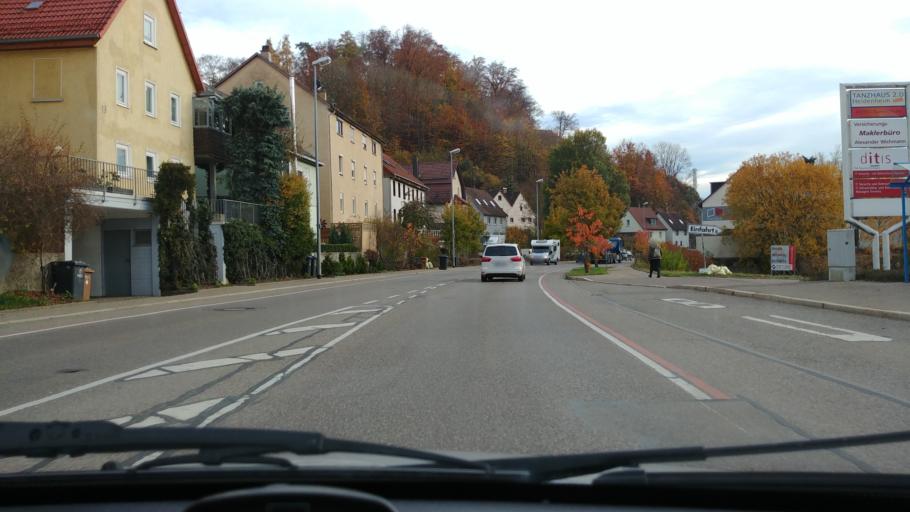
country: DE
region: Baden-Wuerttemberg
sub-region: Regierungsbezirk Stuttgart
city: Heidenheim an der Brenz
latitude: 48.6606
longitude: 10.1593
